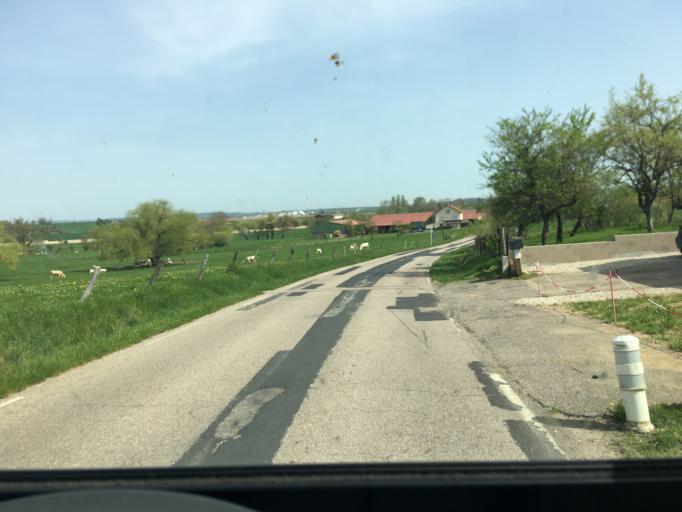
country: FR
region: Lorraine
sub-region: Departement de Meurthe-et-Moselle
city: Art-sur-Meurthe
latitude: 48.6128
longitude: 6.2501
